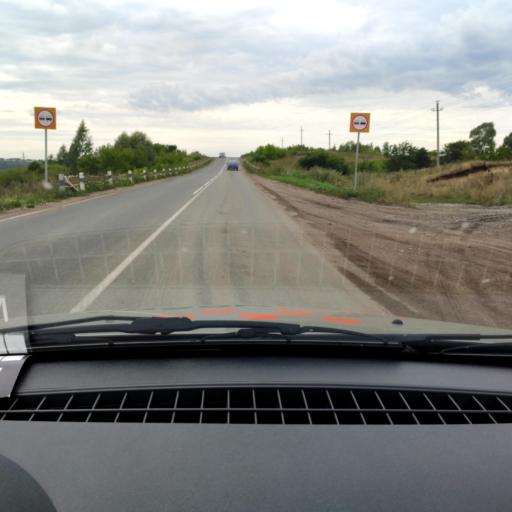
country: RU
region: Bashkortostan
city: Kabakovo
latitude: 54.5868
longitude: 56.2568
